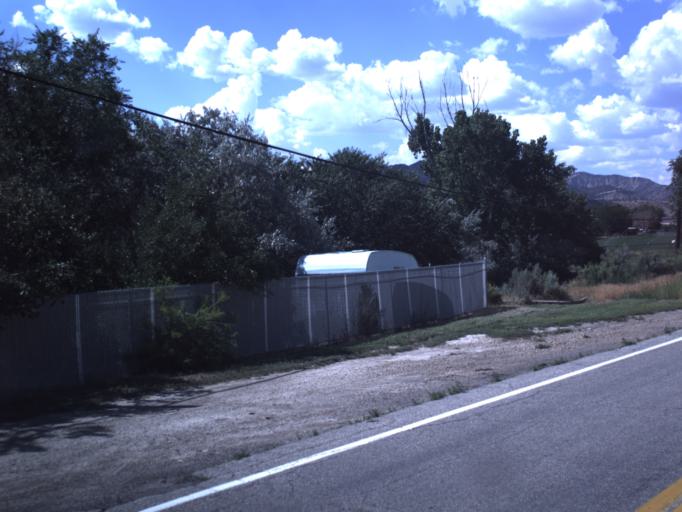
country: US
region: Utah
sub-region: Carbon County
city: Spring Glen
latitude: 39.6547
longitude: -110.8557
